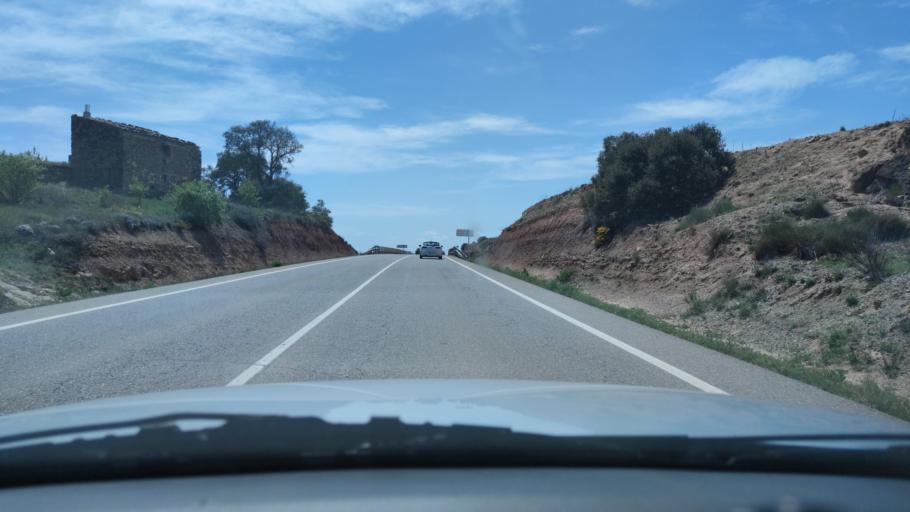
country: ES
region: Catalonia
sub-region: Provincia de Lleida
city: Mont-roig del Camp
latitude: 41.7438
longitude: 1.2245
